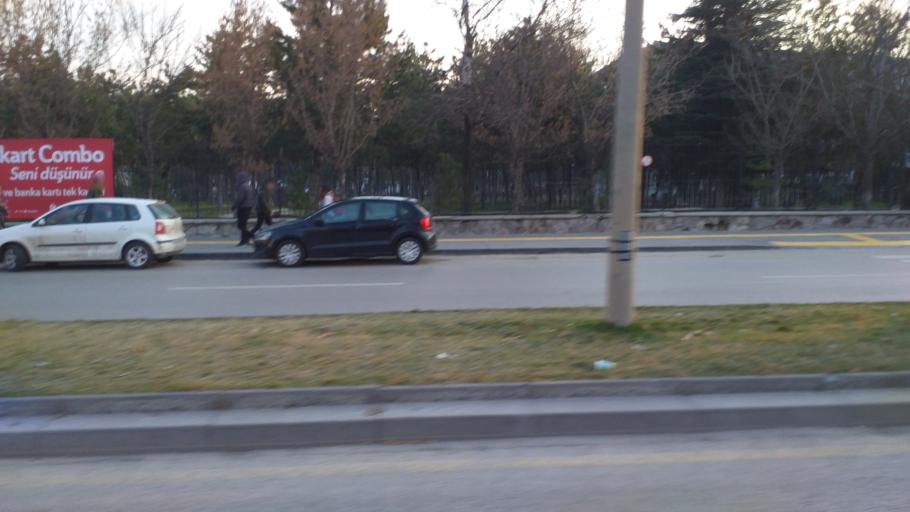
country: TR
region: Ankara
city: Ankara
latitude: 39.9351
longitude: 32.8255
